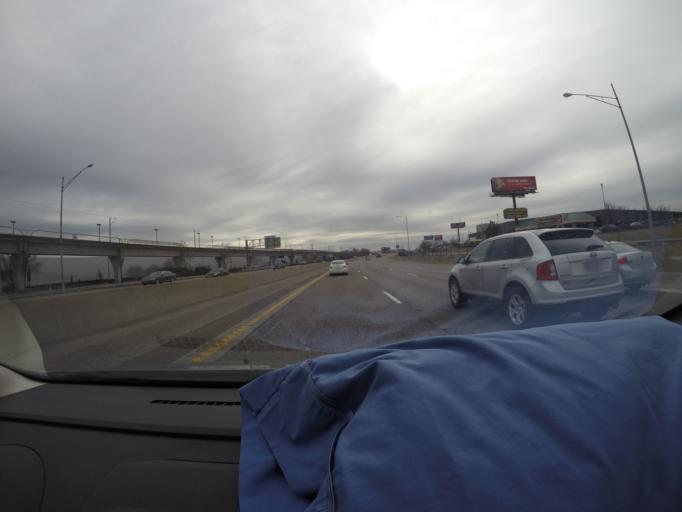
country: US
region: Missouri
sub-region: Saint Louis County
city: Woodson Terrace
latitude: 38.7389
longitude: -90.3633
